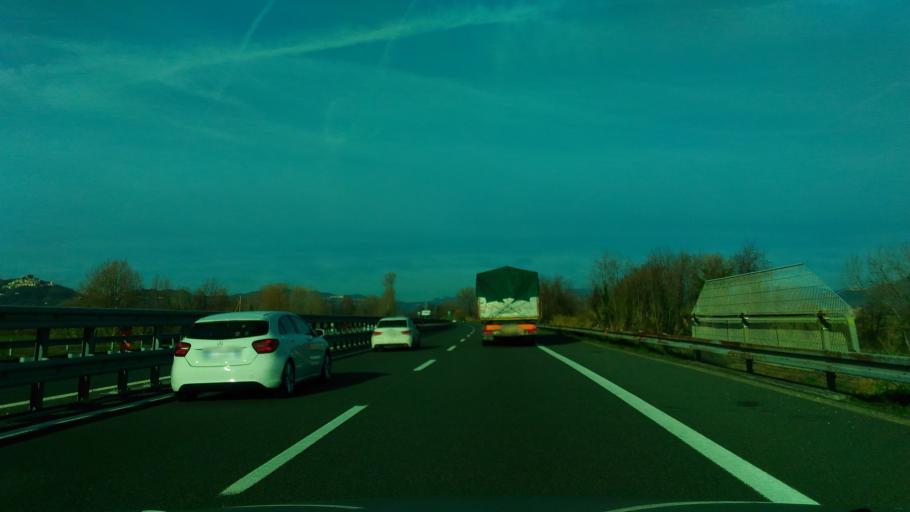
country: IT
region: Liguria
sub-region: Provincia di La Spezia
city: Sarzana
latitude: 44.0921
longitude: 9.9689
